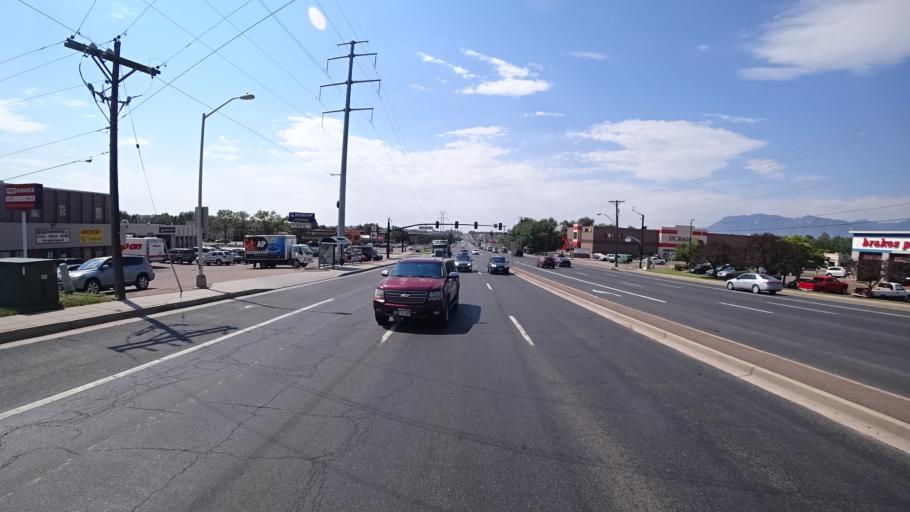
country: US
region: Colorado
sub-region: El Paso County
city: Stratmoor
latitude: 38.8326
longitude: -104.7574
